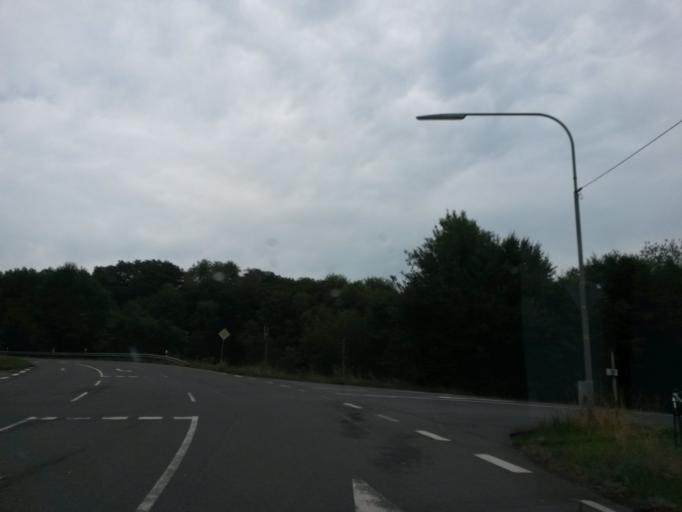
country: DE
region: North Rhine-Westphalia
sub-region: Regierungsbezirk Koln
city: Numbrecht
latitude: 50.8760
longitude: 7.5313
